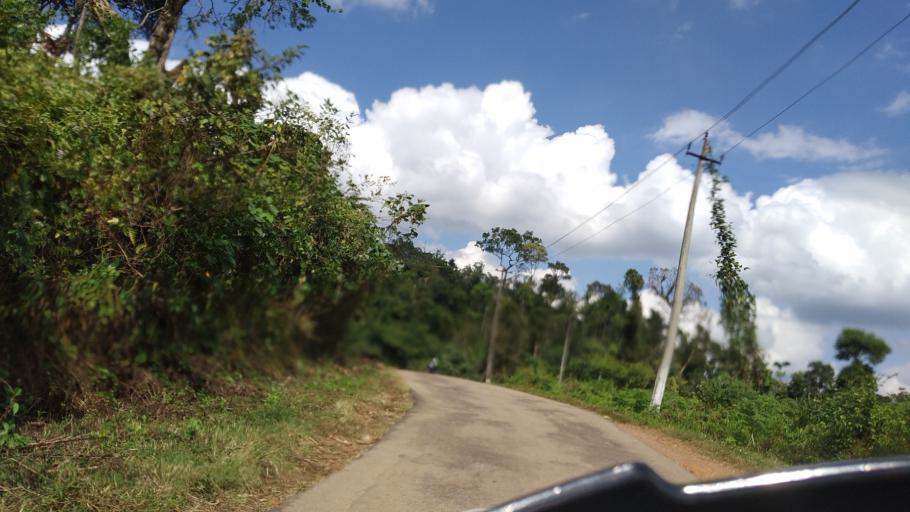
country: IN
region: Karnataka
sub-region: Kodagu
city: Ponnampet
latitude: 12.0293
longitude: 75.8961
